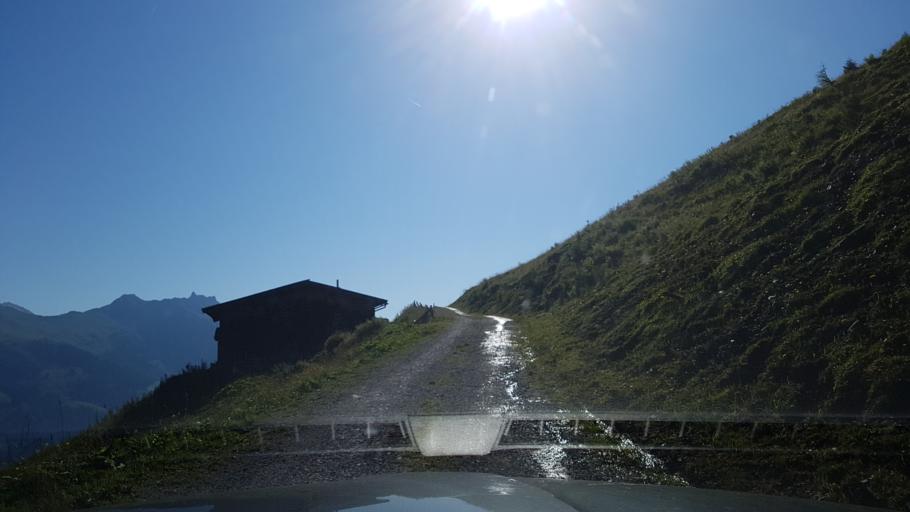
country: AT
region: Salzburg
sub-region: Politischer Bezirk Sankt Johann im Pongau
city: Dorfgastein
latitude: 47.2442
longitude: 13.0652
